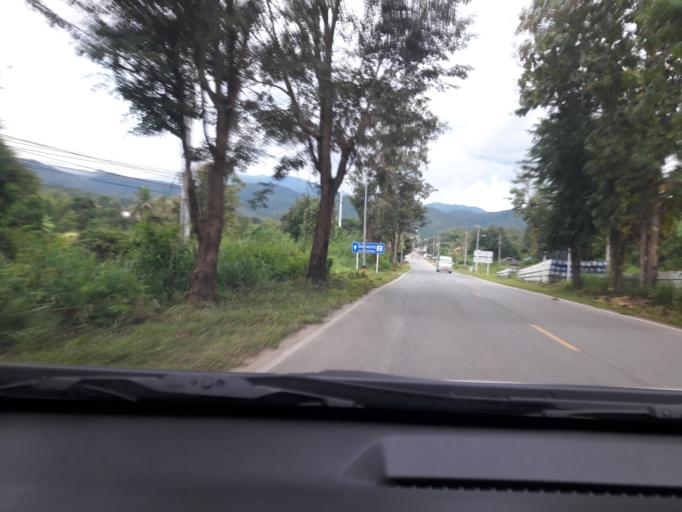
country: TH
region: Mae Hong Son
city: Mae Hi
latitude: 19.3021
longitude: 98.4622
